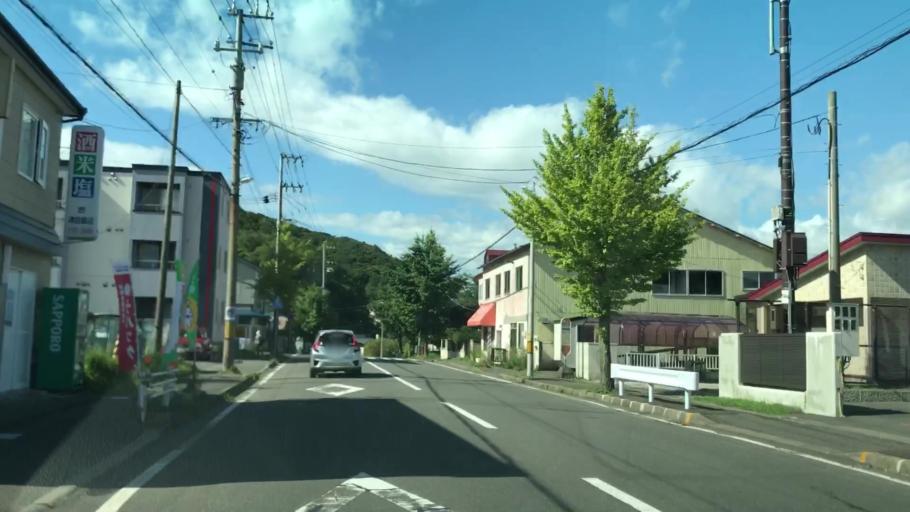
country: JP
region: Hokkaido
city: Muroran
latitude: 42.3250
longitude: 140.9678
